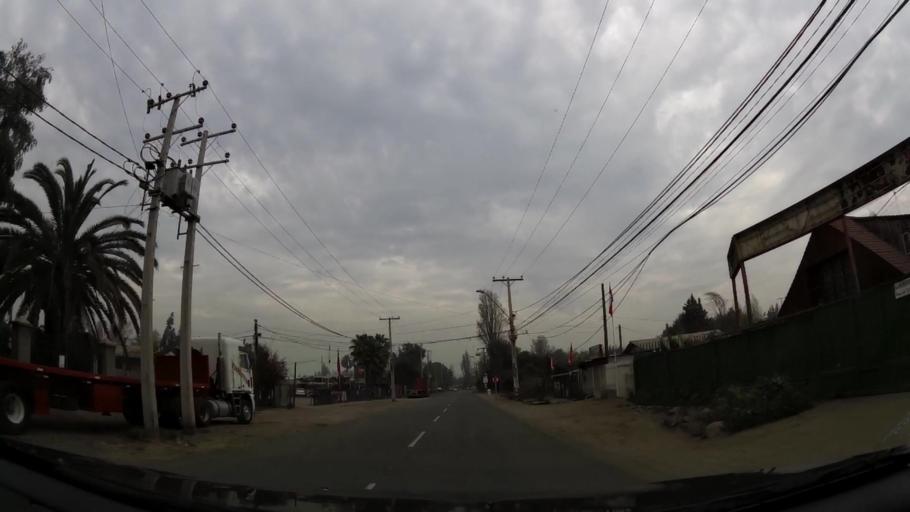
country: CL
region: Santiago Metropolitan
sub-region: Provincia de Chacabuco
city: Chicureo Abajo
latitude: -33.2717
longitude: -70.7444
